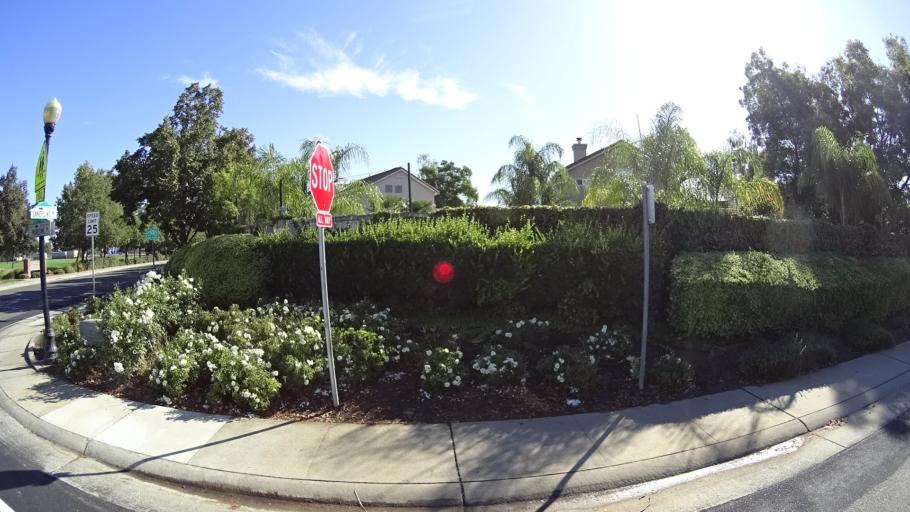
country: US
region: California
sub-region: Sacramento County
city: Laguna
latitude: 38.4098
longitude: -121.4638
